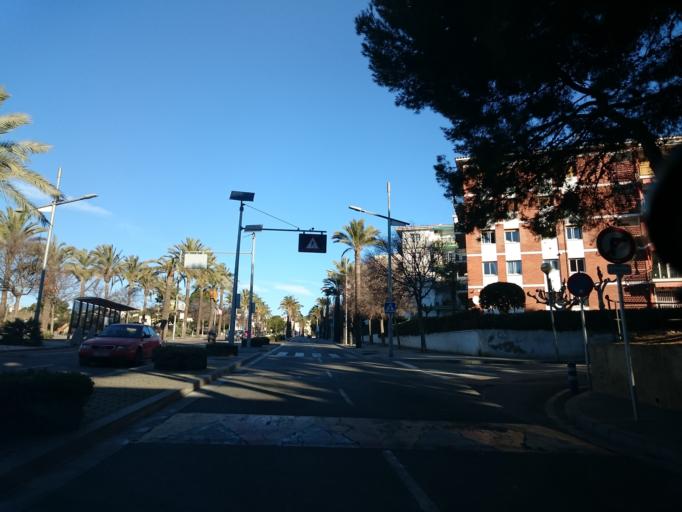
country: ES
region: Catalonia
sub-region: Provincia de Barcelona
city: Sitges
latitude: 41.2396
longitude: 1.8066
